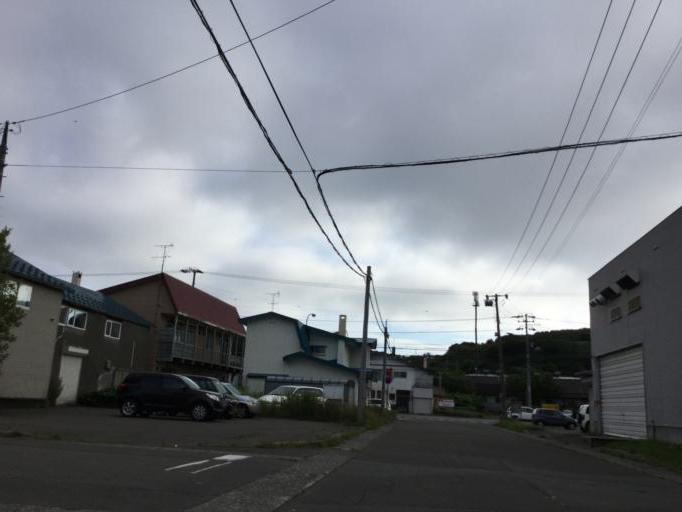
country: JP
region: Hokkaido
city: Wakkanai
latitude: 45.4031
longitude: 141.6787
